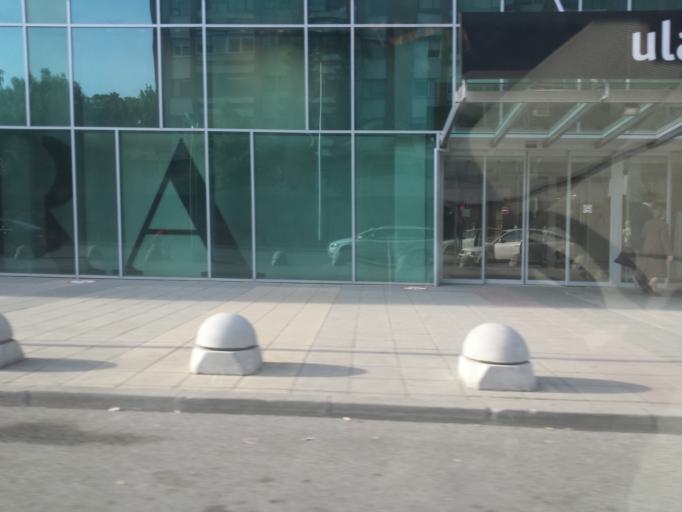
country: HR
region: Grad Zagreb
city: Novi Zagreb
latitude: 45.7758
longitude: 15.9786
